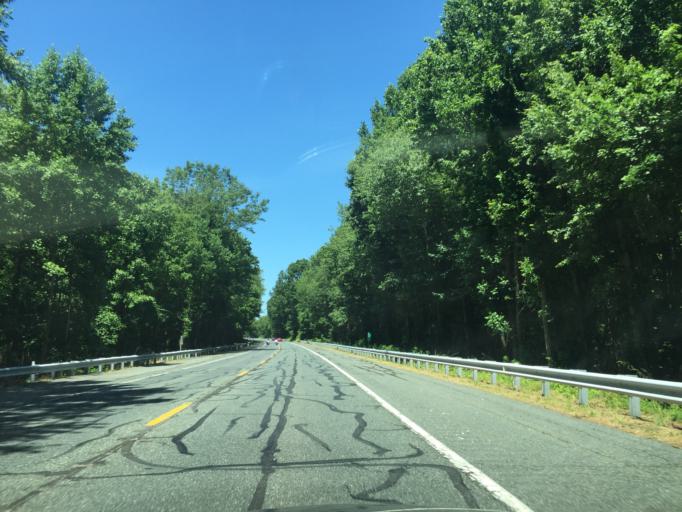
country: US
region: Maryland
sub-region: Harford County
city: Jarrettsville
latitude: 39.5859
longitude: -76.4611
